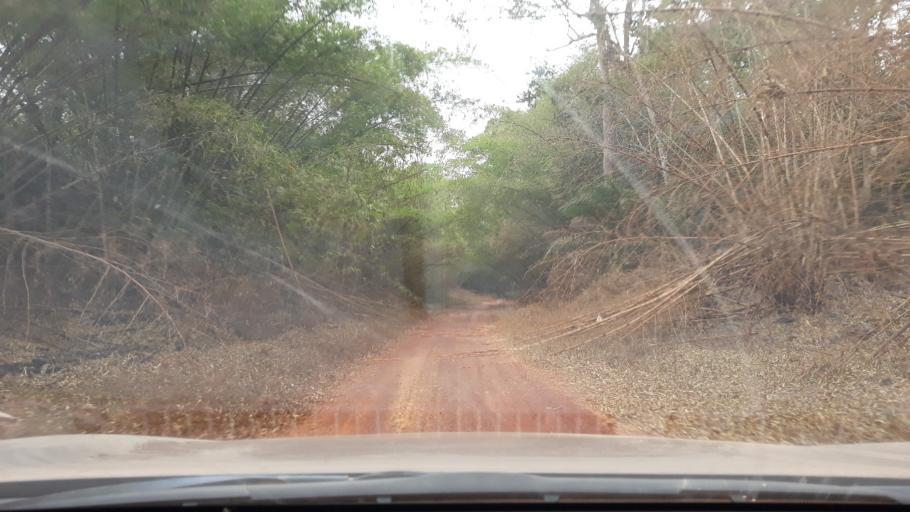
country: CD
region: Eastern Province
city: Buta
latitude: 2.2863
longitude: 25.0557
